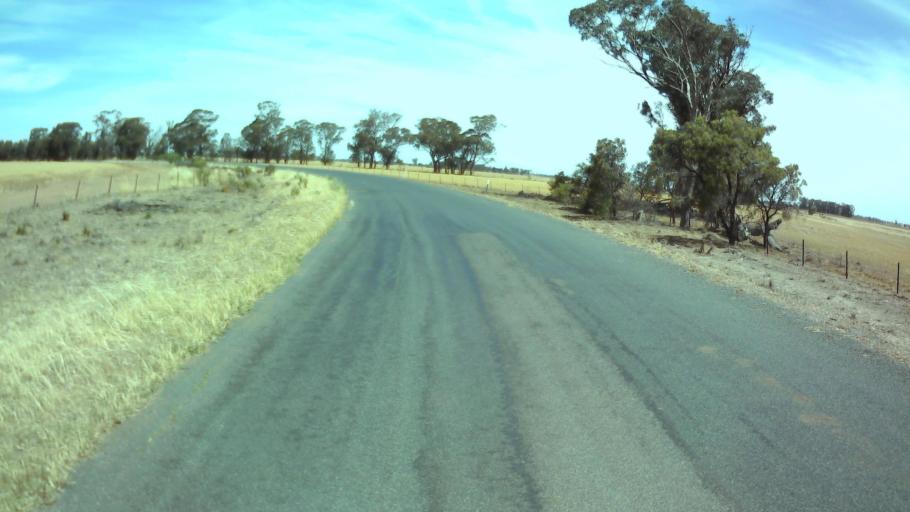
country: AU
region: New South Wales
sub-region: Weddin
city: Grenfell
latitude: -33.9549
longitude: 147.7771
